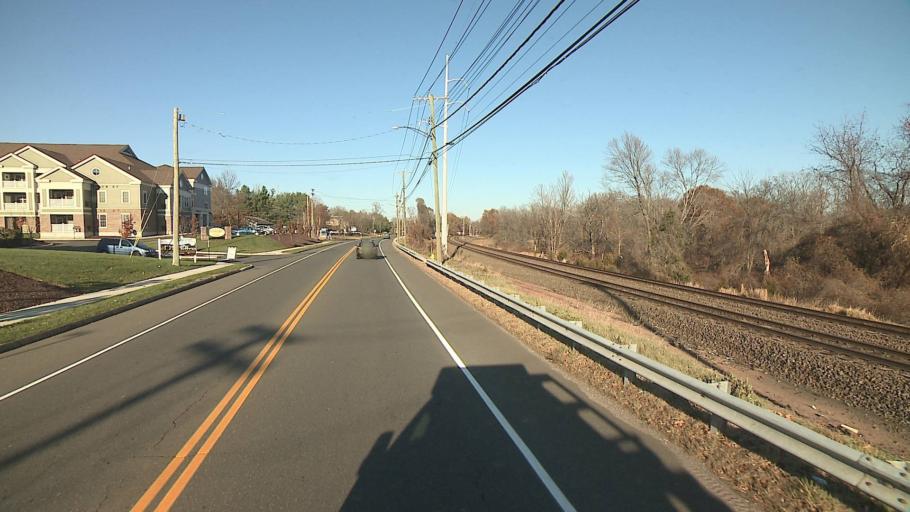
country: US
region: Connecticut
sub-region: New Haven County
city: North Haven
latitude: 41.3810
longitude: -72.8768
